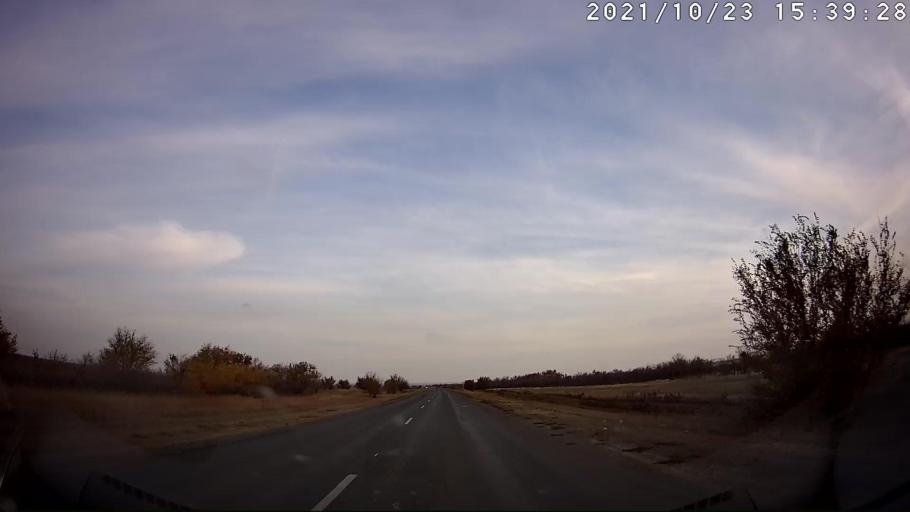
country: RU
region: Volgograd
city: Bereslavka
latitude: 48.1234
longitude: 44.1279
